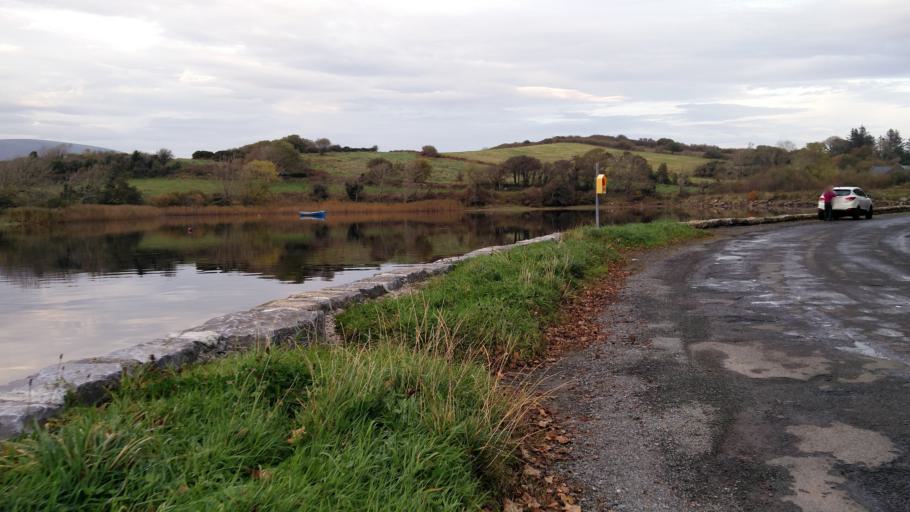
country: IE
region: Connaught
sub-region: Maigh Eo
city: Westport
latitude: 53.8857
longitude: -9.5564
